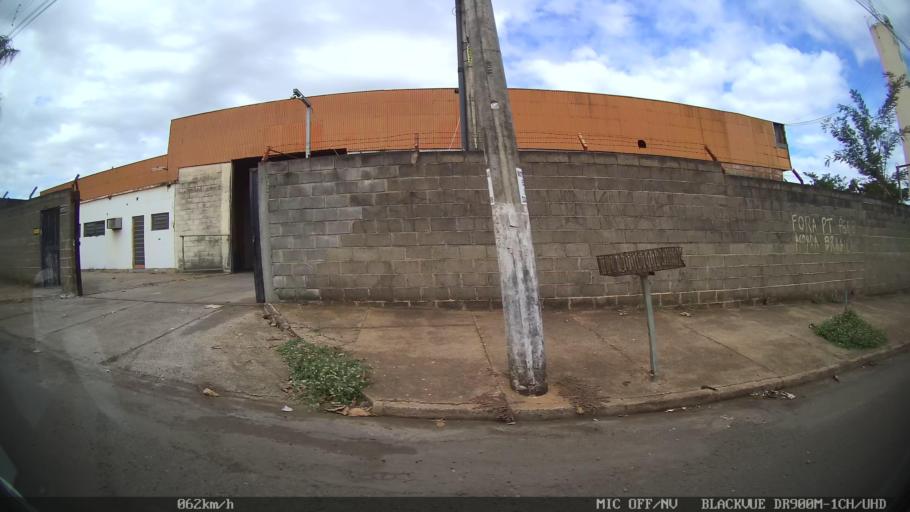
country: BR
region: Sao Paulo
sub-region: Sao Jose Do Rio Preto
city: Sao Jose do Rio Preto
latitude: -20.8107
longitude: -49.4947
